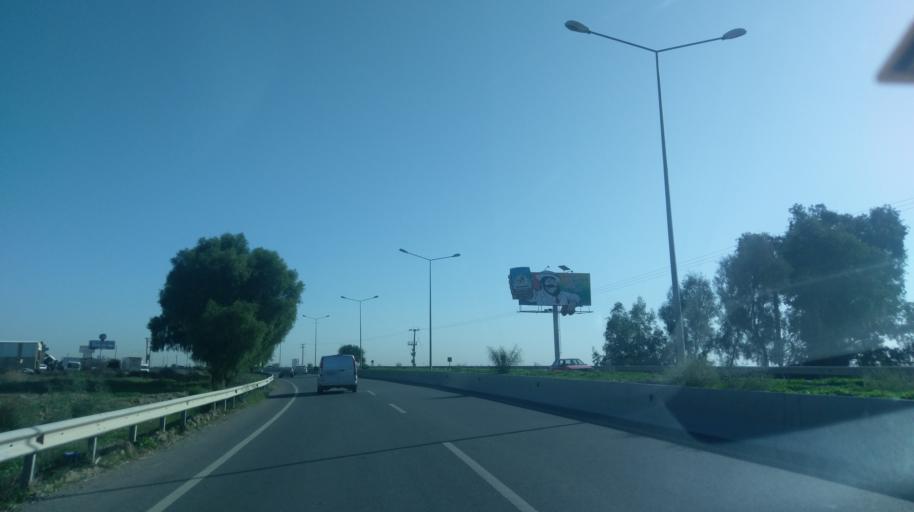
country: CY
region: Lefkosia
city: Nicosia
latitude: 35.2137
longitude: 33.4453
